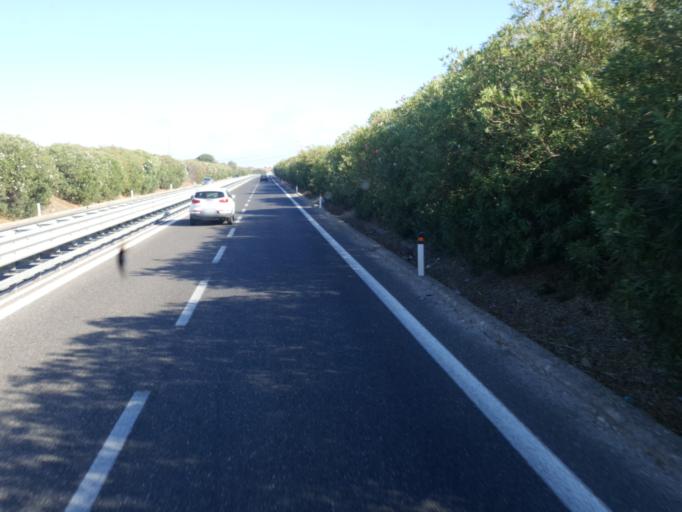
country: IT
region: Latium
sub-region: Provincia di Viterbo
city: Pescia Romana
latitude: 42.3833
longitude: 11.5489
